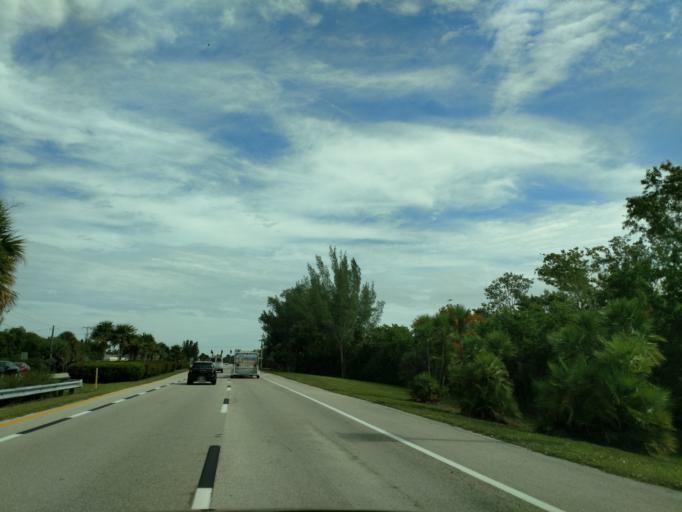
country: US
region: Florida
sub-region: Lee County
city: Punta Rassa
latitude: 26.4909
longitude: -81.9843
